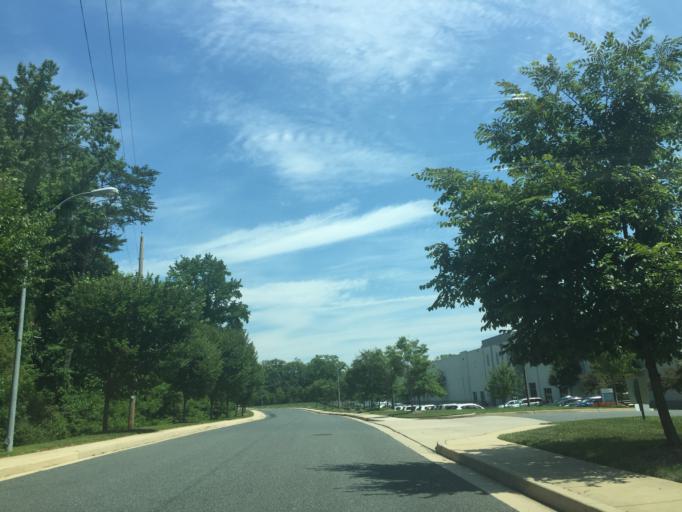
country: US
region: Maryland
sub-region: Baltimore County
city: Middle River
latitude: 39.3438
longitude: -76.4225
